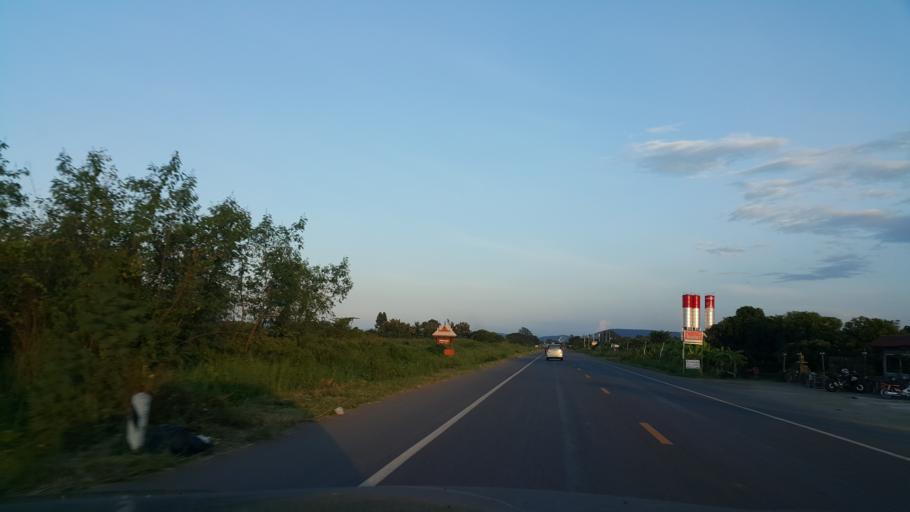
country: TH
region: Lamphun
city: Pa Sang
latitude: 18.4883
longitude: 98.9256
